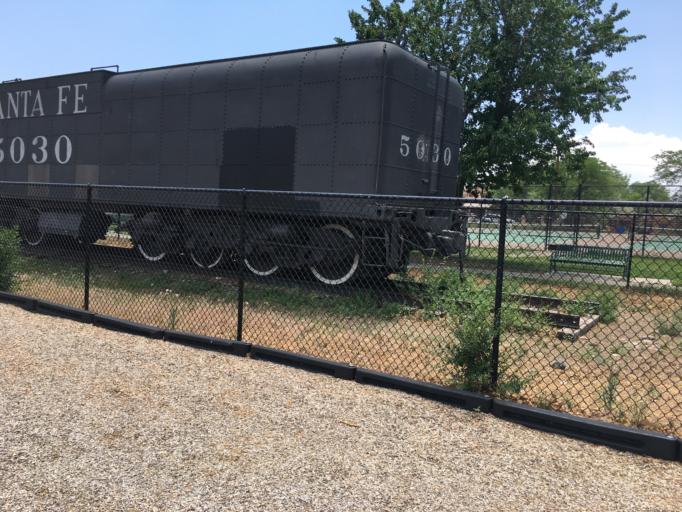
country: US
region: New Mexico
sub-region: Santa Fe County
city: Santa Fe
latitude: 35.6714
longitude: -105.9529
